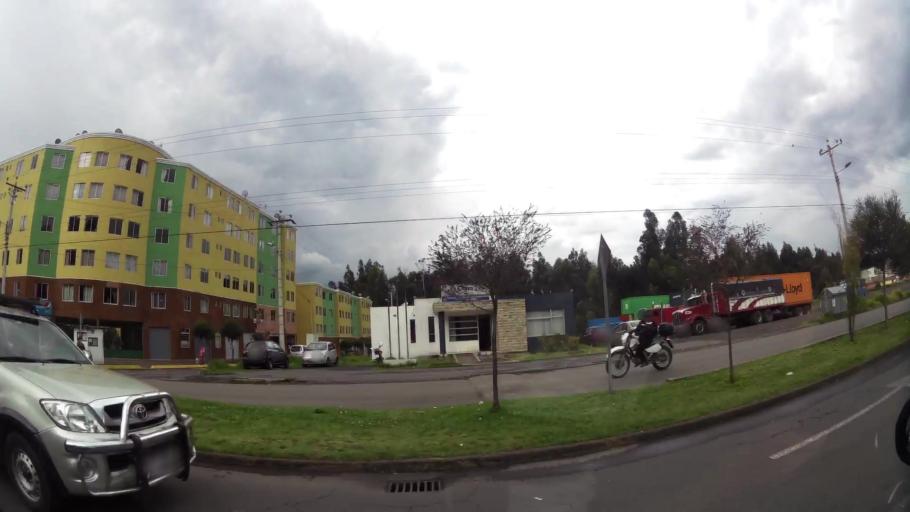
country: EC
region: Pichincha
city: Quito
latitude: -0.2926
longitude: -78.5512
